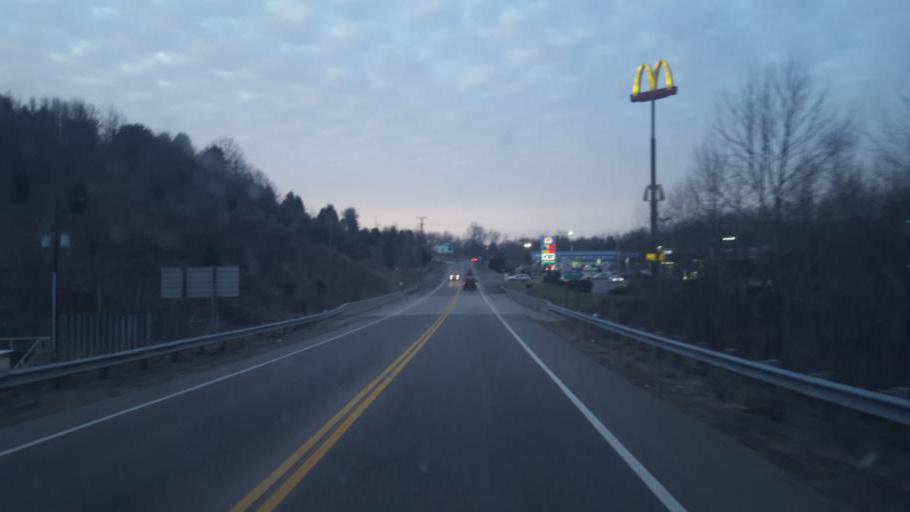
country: US
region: Ohio
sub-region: Jackson County
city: Oak Hill
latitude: 38.8898
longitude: -82.3825
